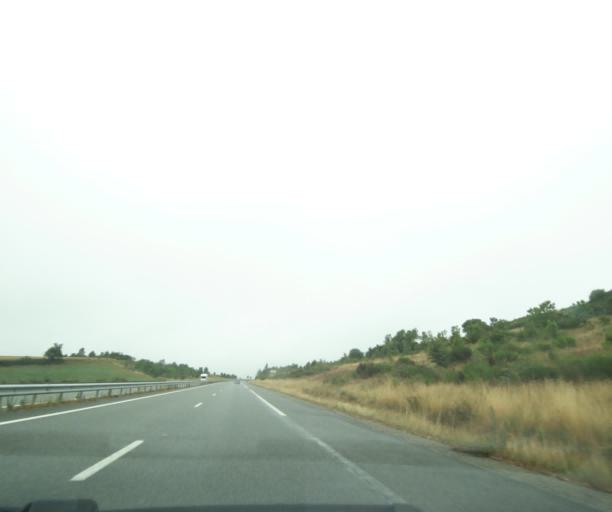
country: FR
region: Midi-Pyrenees
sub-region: Departement de l'Aveyron
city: Naucelle
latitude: 44.1248
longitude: 2.3092
